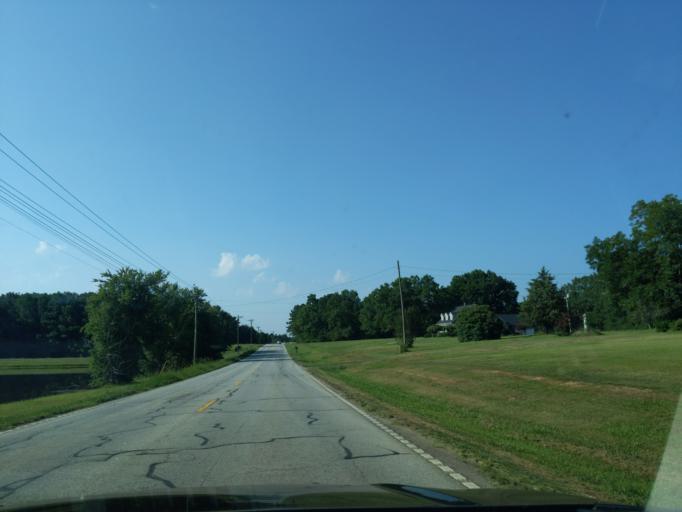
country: US
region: South Carolina
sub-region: Newberry County
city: Prosperity
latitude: 34.1738
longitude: -81.5341
